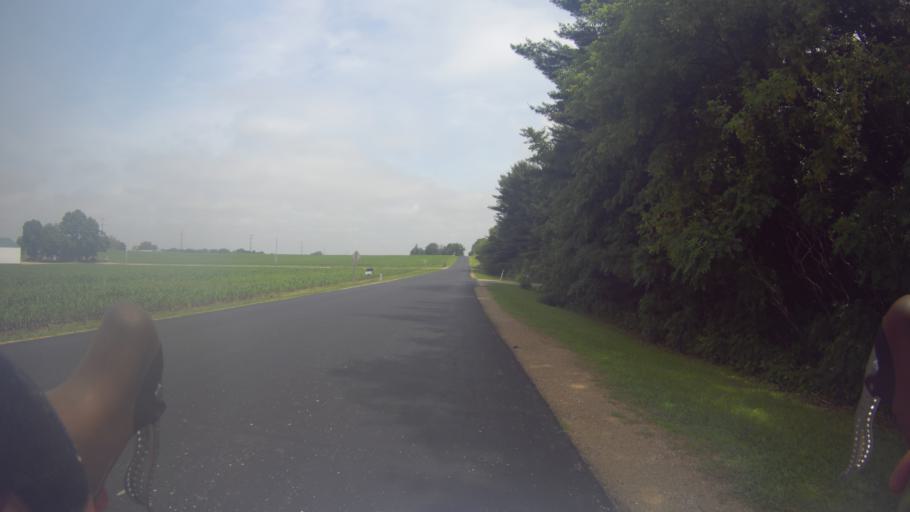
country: US
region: Wisconsin
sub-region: Rock County
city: Edgerton
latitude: 42.8972
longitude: -89.0426
